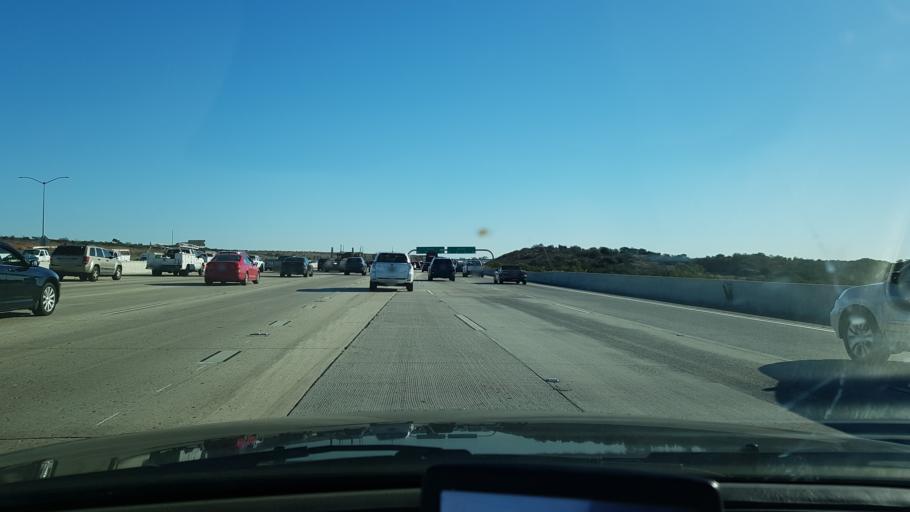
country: US
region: California
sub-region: San Diego County
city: Poway
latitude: 32.8730
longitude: -117.1077
